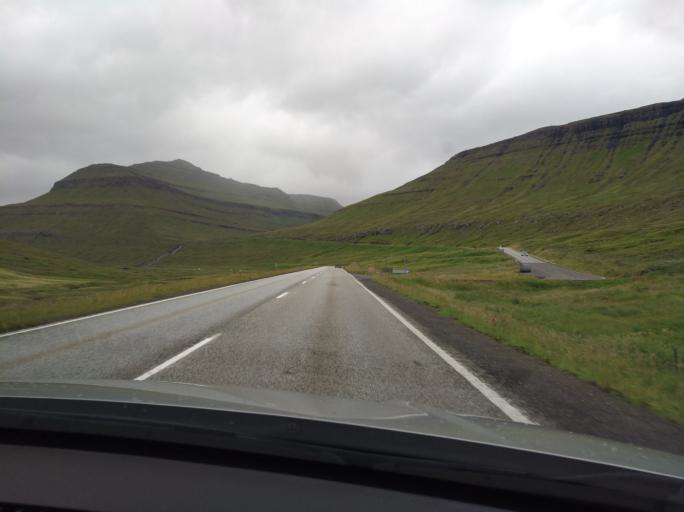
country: FO
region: Eysturoy
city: Fuglafjordur
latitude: 62.2107
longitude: -6.8627
